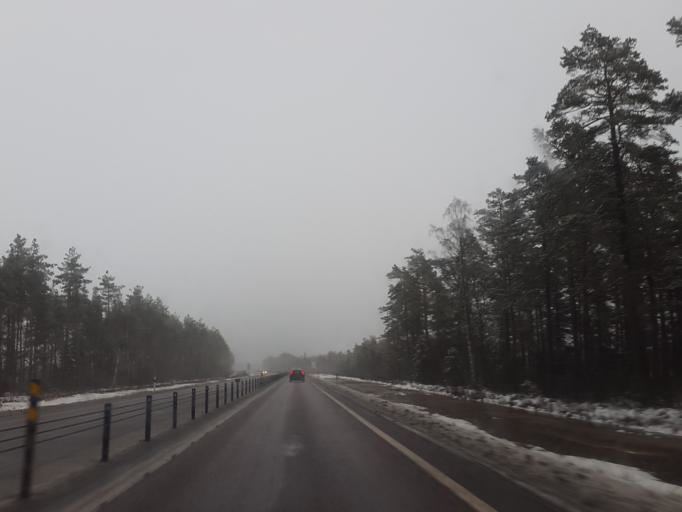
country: SE
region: Joenkoeping
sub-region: Jonkopings Kommun
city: Taberg
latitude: 57.7638
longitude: 14.0160
